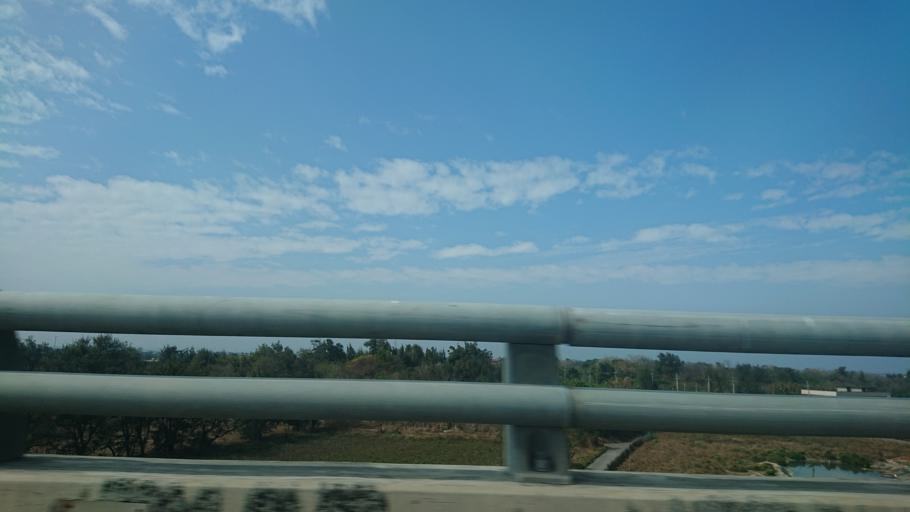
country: TW
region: Taiwan
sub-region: Yunlin
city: Douliu
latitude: 23.8569
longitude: 120.2961
